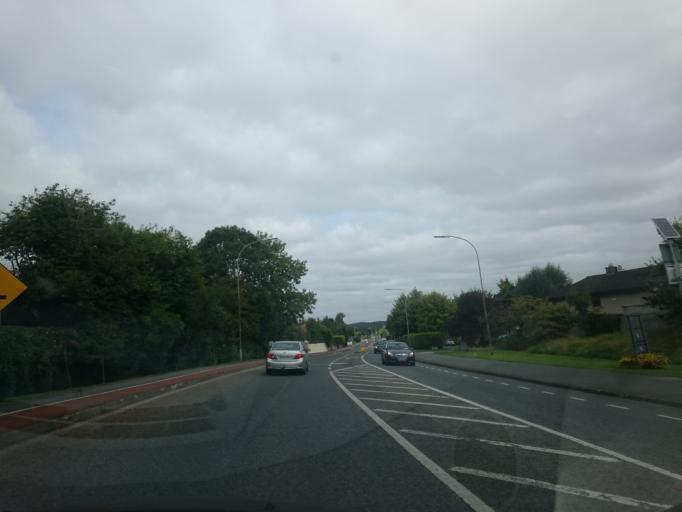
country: IE
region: Leinster
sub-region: Kilkenny
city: Kilkenny
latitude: 52.6719
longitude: -7.2536
